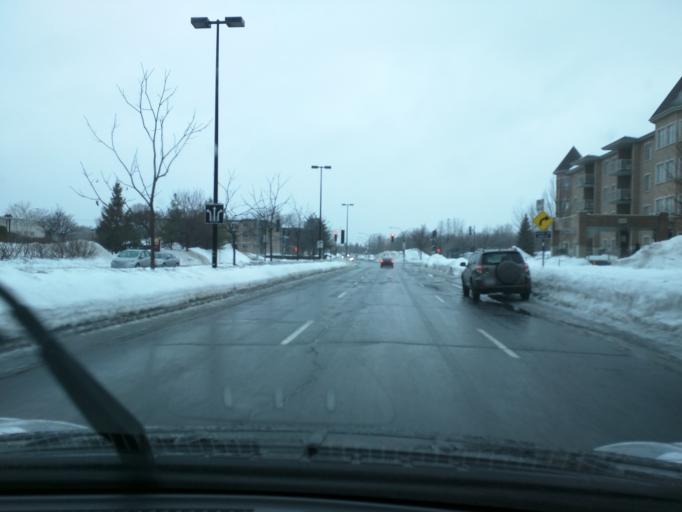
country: CA
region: Quebec
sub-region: Monteregie
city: Longueuil
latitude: 45.5413
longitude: -73.4703
